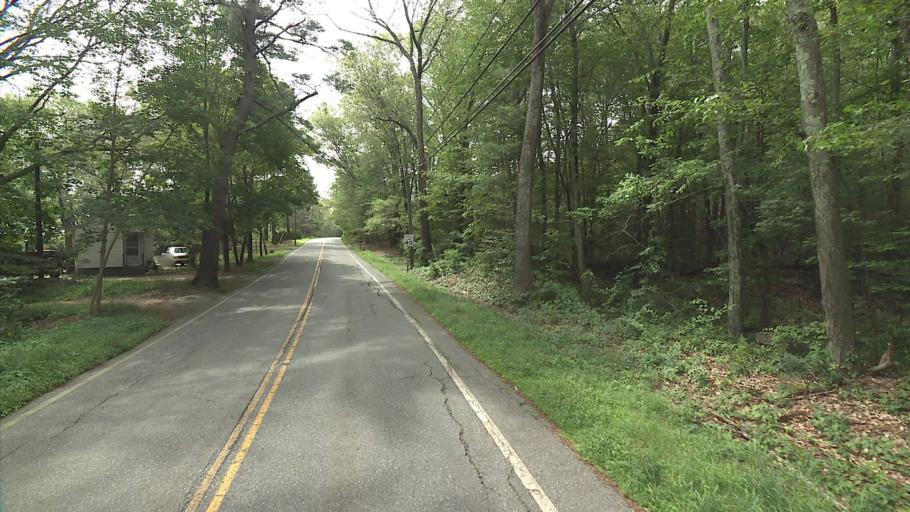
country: US
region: Massachusetts
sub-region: Worcester County
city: Webster
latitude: 42.0153
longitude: -71.8450
